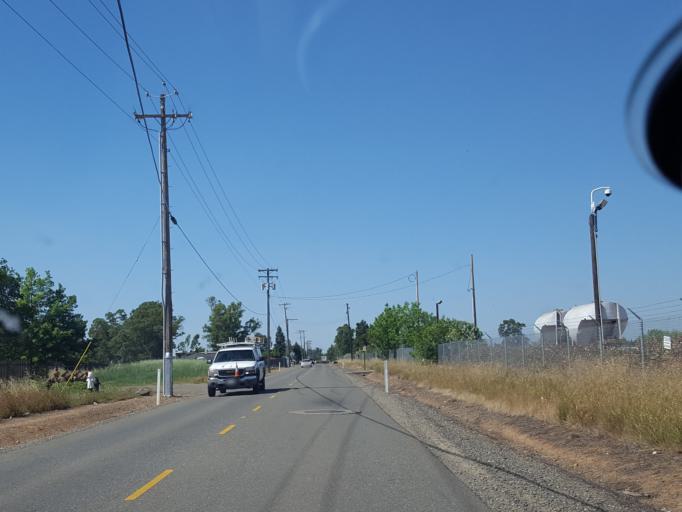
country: US
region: California
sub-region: Sacramento County
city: La Riviera
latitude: 38.5499
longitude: -121.3217
